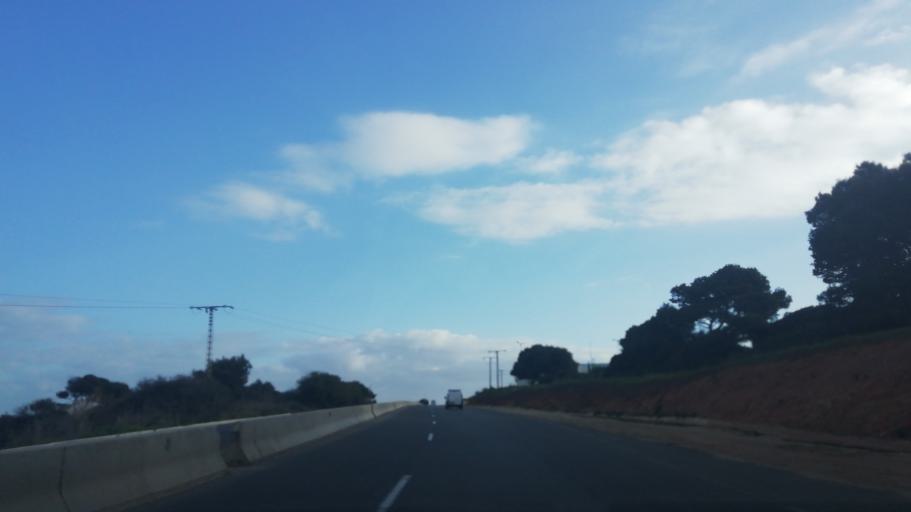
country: DZ
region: Mostaganem
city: Mostaganem
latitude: 36.0969
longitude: 0.2841
